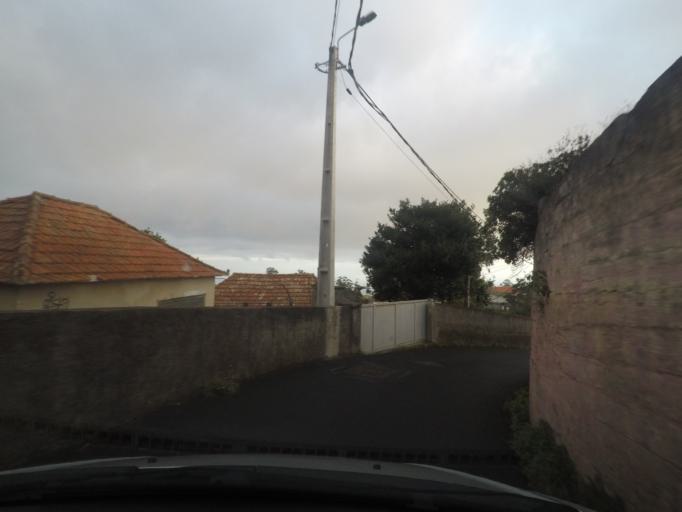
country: PT
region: Madeira
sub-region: Santa Cruz
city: Camacha
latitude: 32.6800
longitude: -16.8488
